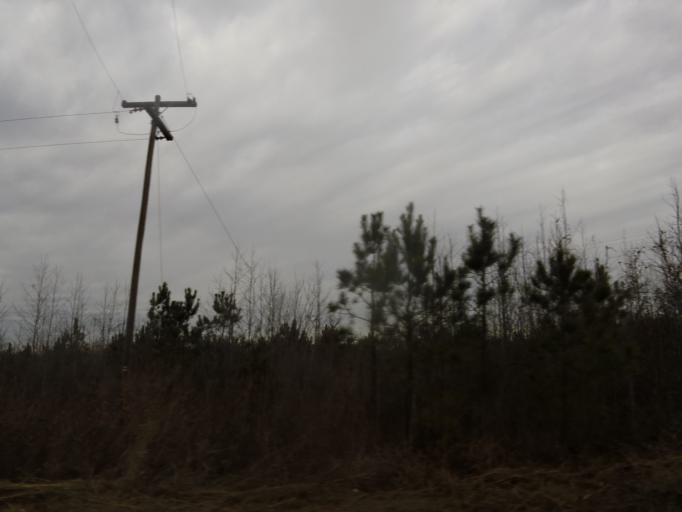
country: US
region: North Carolina
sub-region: Halifax County
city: Scotland Neck
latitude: 36.2525
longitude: -77.3171
